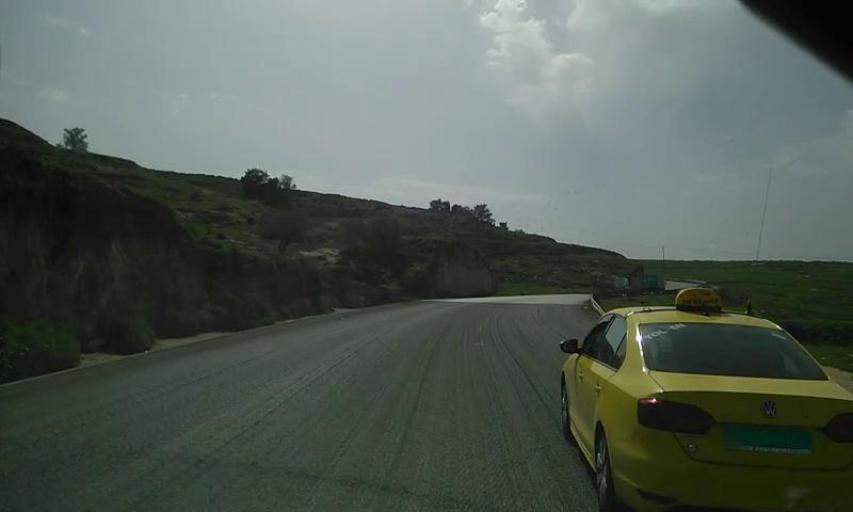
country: PS
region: West Bank
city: `Anzah
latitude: 32.3826
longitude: 35.2173
